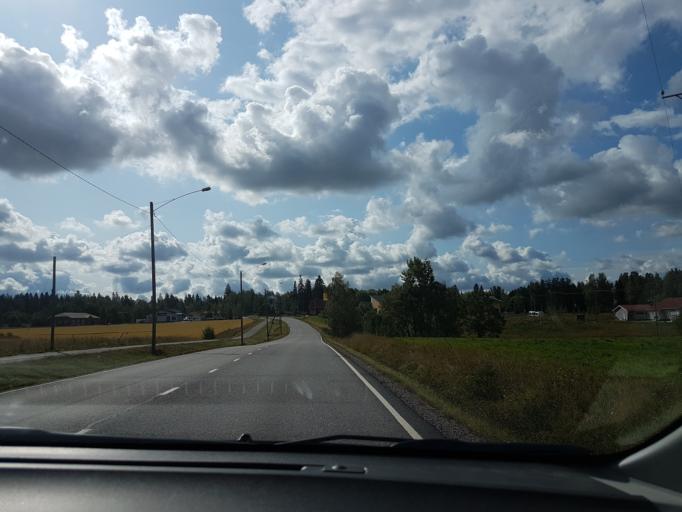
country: FI
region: Uusimaa
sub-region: Helsinki
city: Pornainen
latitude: 60.4828
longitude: 25.3698
